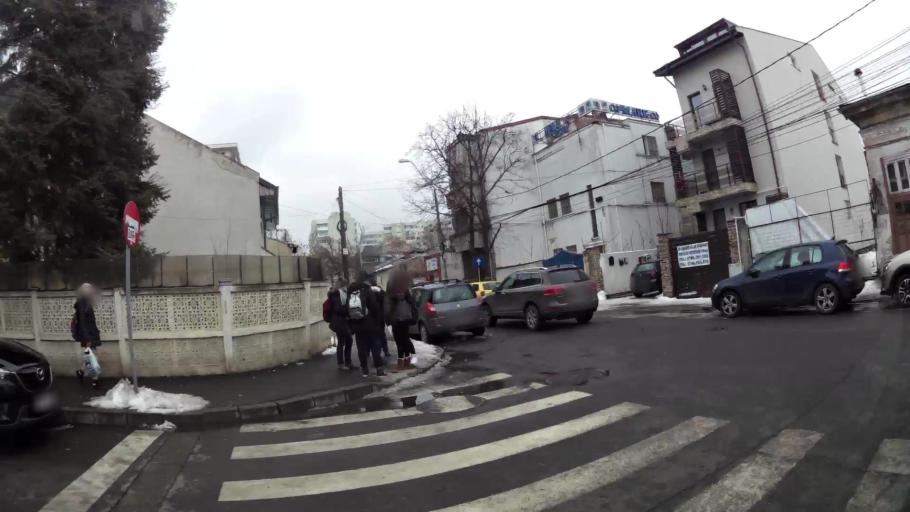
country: RO
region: Bucuresti
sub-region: Municipiul Bucuresti
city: Bucuresti
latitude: 44.4546
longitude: 26.0714
